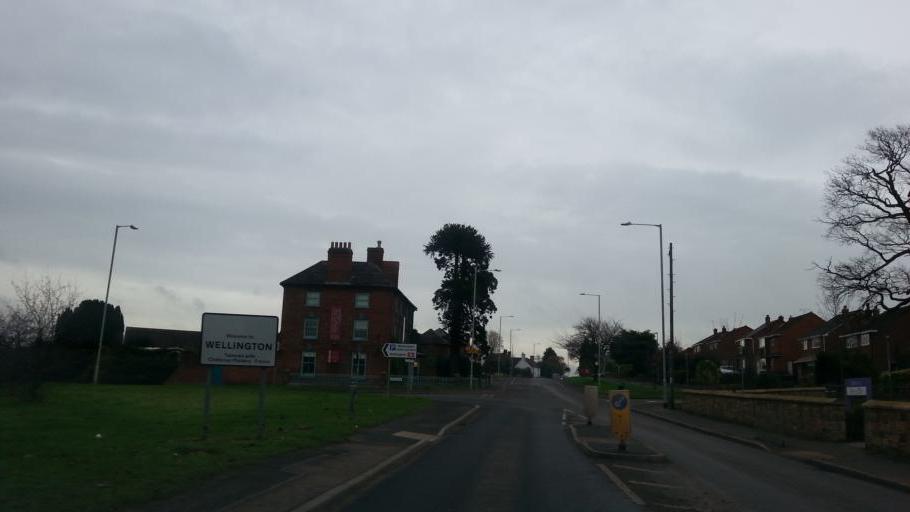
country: GB
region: England
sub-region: Telford and Wrekin
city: Wellington
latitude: 52.6929
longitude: -2.5355
